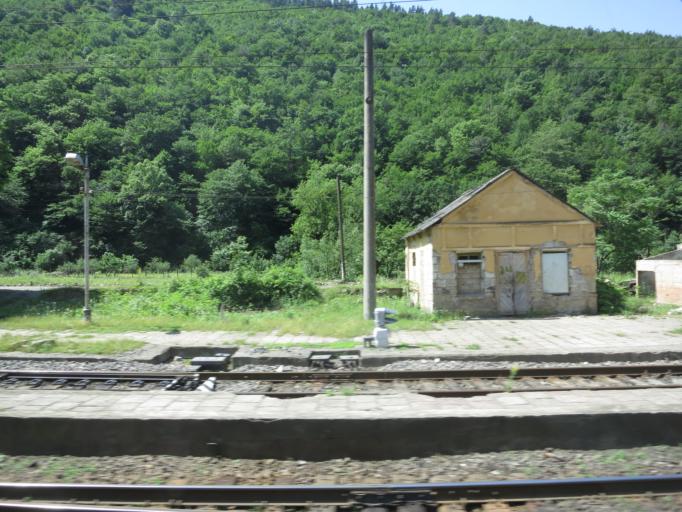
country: GE
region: Imereti
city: Kharagauli
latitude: 41.9753
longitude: 43.2976
